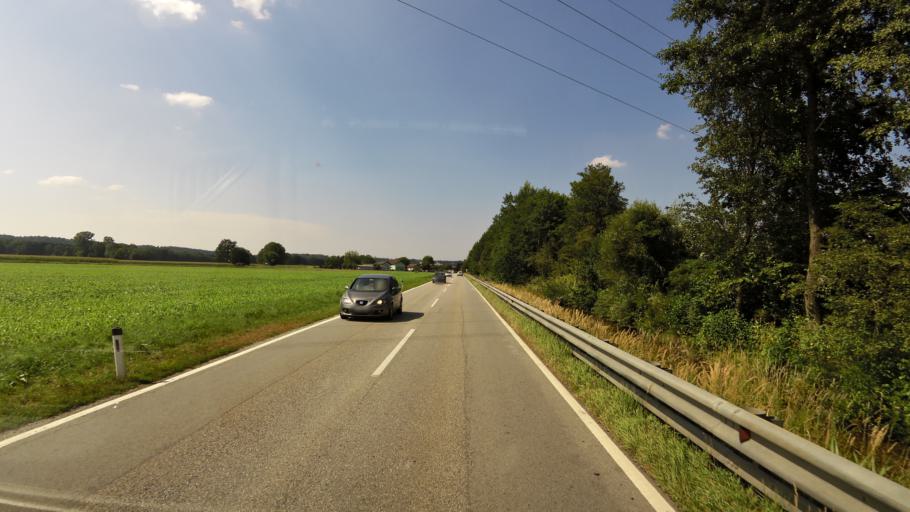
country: AT
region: Upper Austria
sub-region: Politischer Bezirk Braunau am Inn
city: Altheim
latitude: 48.1356
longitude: 13.1406
